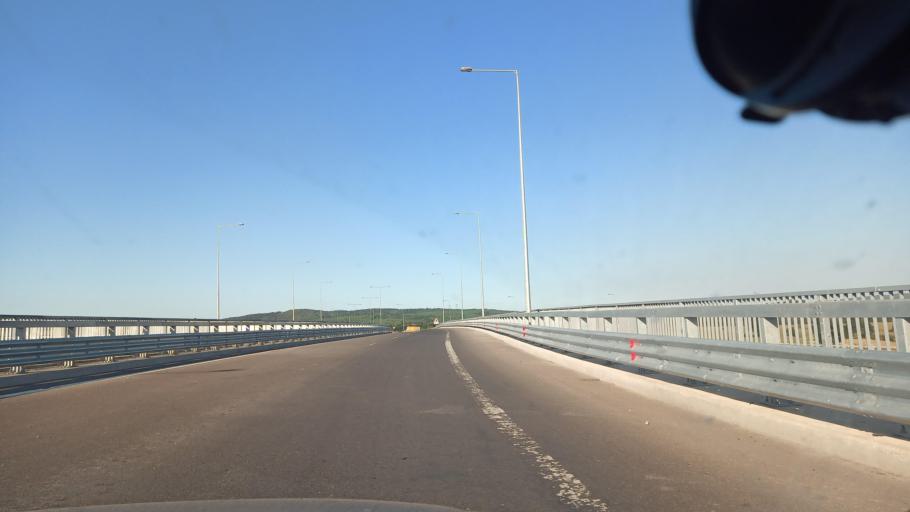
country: TR
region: Sakarya
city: Kazimpasa
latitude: 40.8271
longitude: 30.3495
